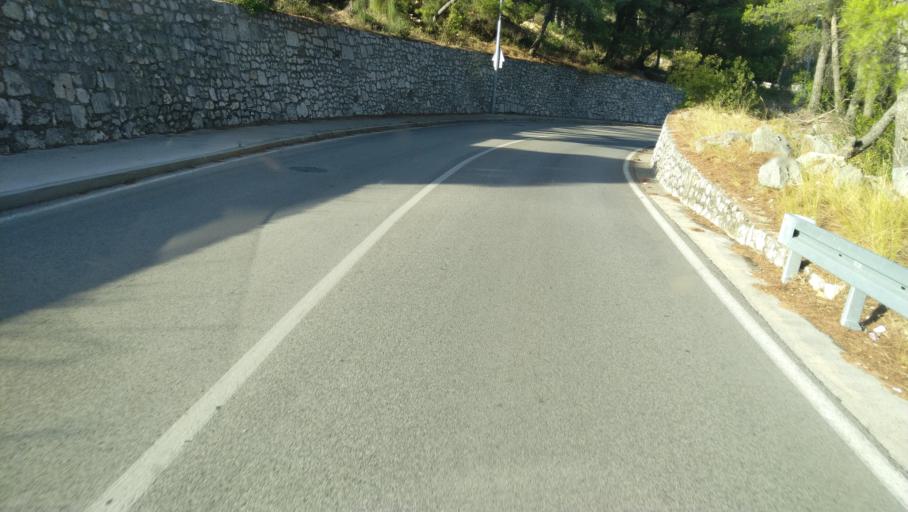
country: HR
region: Sibensko-Kniniska
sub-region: Grad Sibenik
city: Sibenik
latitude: 43.7473
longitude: 15.8941
